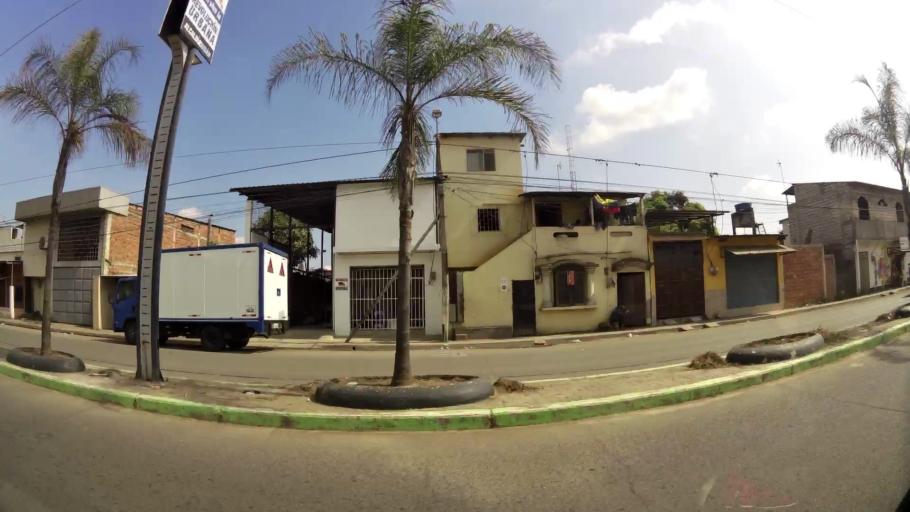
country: EC
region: Guayas
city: Eloy Alfaro
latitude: -2.1576
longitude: -79.8300
